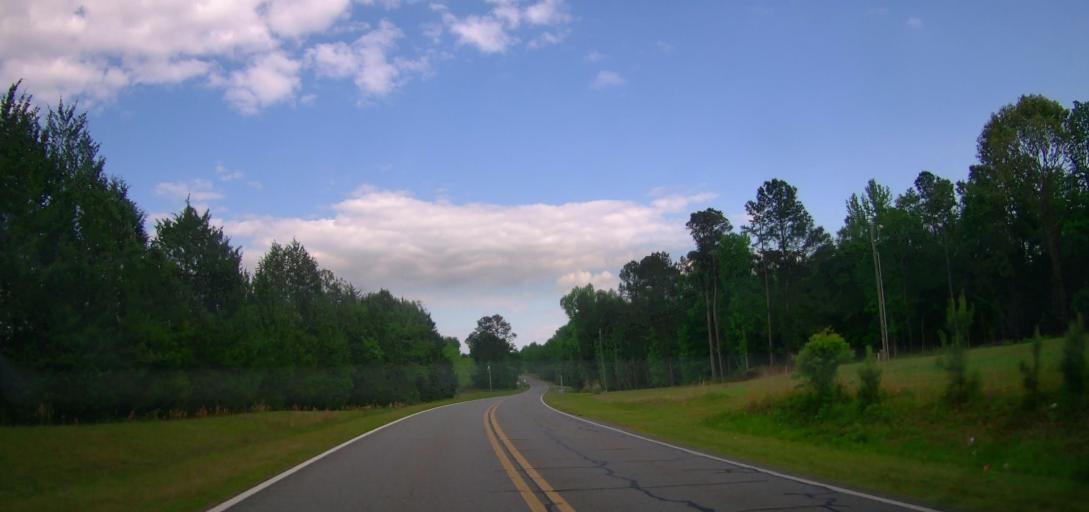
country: US
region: Georgia
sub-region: Baldwin County
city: Hardwick
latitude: 33.0623
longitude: -83.1383
